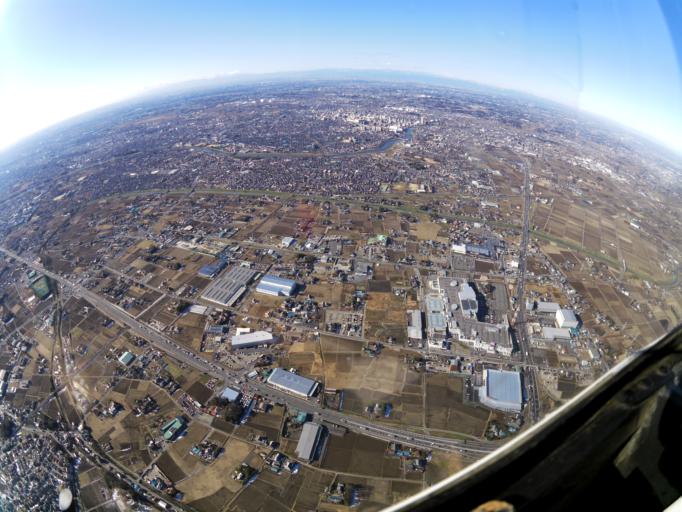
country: JP
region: Saitama
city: Kasukabe
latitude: 35.9867
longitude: 139.7972
